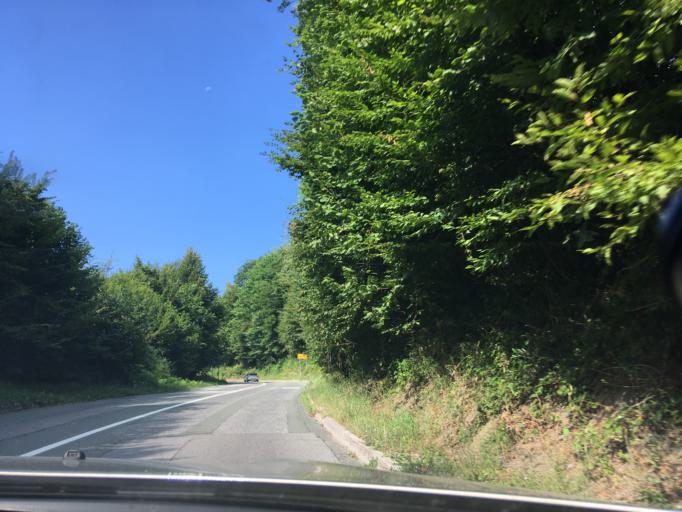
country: HR
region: Primorsko-Goranska
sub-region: Grad Delnice
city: Delnice
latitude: 45.4290
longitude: 14.8367
